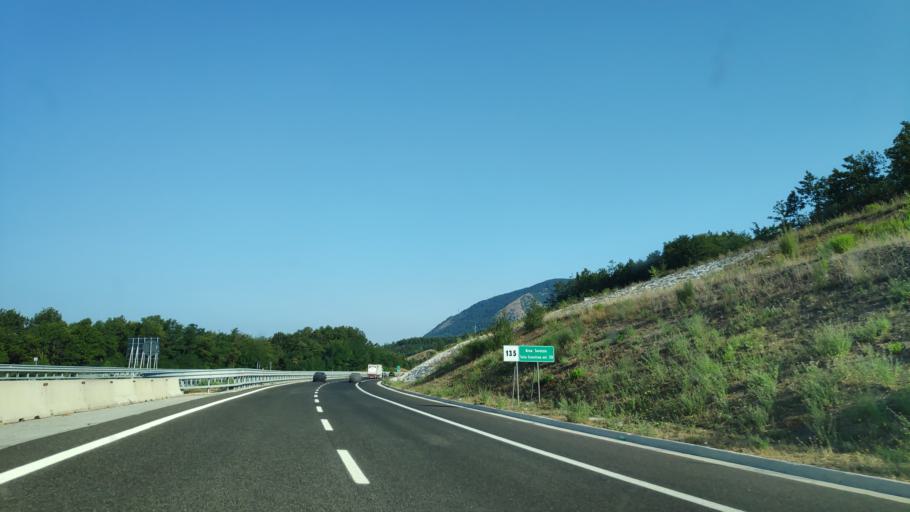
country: IT
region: Basilicate
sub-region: Provincia di Potenza
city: Nemoli
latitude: 40.1031
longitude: 15.7975
